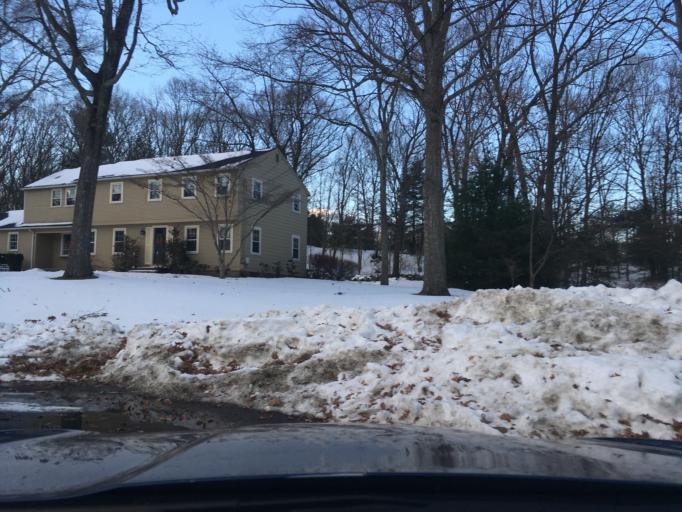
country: US
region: Rhode Island
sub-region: Kent County
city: East Greenwich
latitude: 41.6380
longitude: -71.4711
